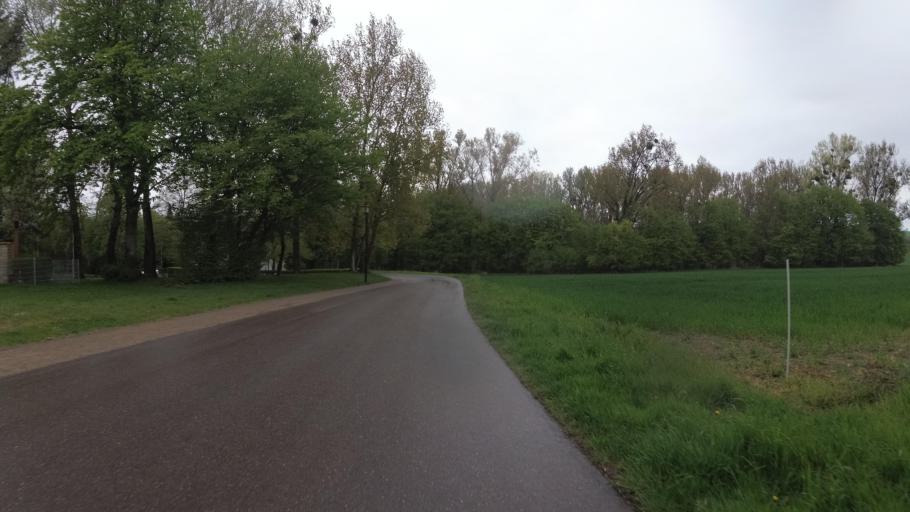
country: FR
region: Lorraine
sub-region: Departement de la Moselle
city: Merten
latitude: 49.2713
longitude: 6.6770
